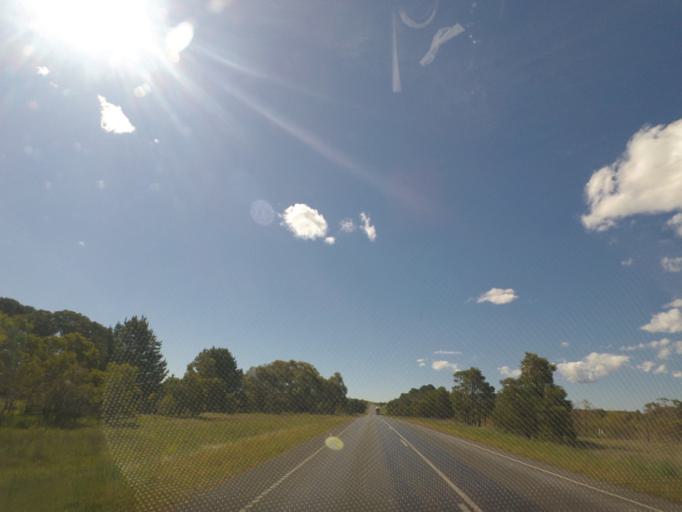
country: AU
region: Victoria
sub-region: Moorabool
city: Bacchus Marsh
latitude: -37.6535
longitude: 144.2296
